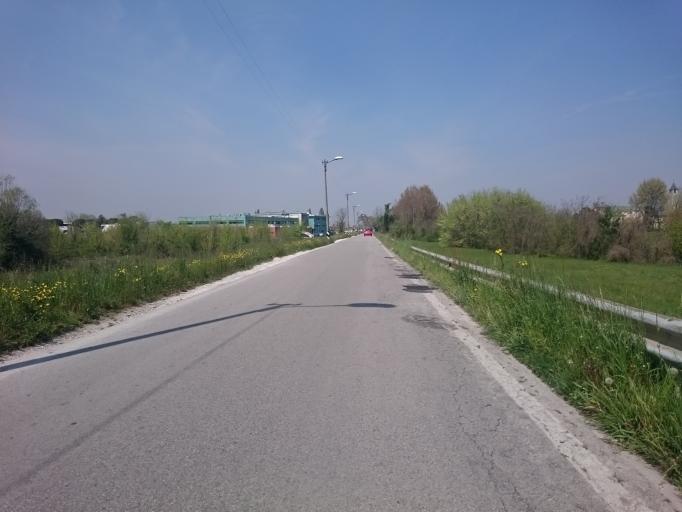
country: IT
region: Veneto
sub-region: Provincia di Padova
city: Tencarola
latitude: 45.3876
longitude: 11.8092
